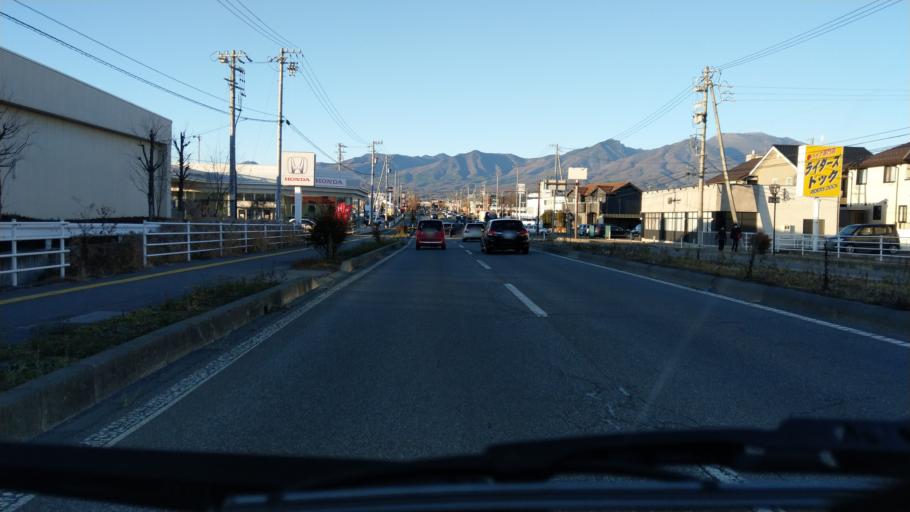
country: JP
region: Nagano
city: Saku
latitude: 36.2673
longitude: 138.4665
